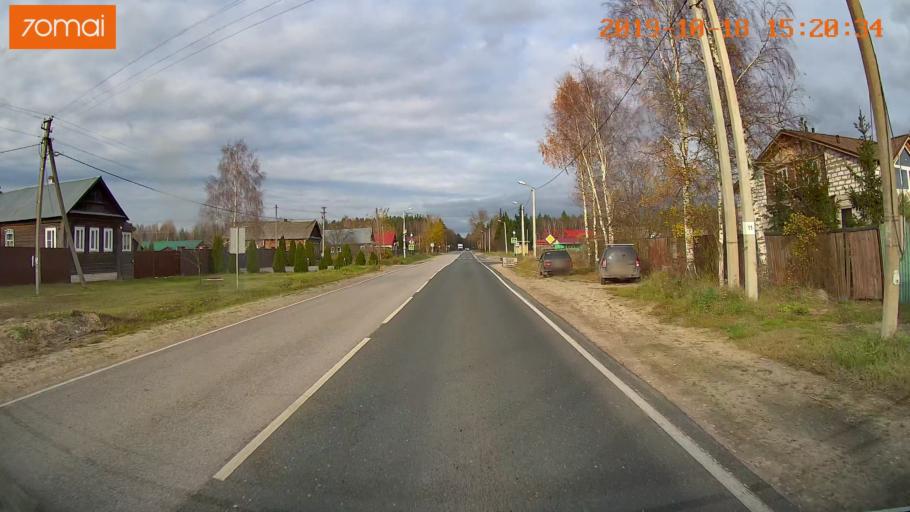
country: RU
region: Vladimir
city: Anopino
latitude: 55.6884
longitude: 40.7454
